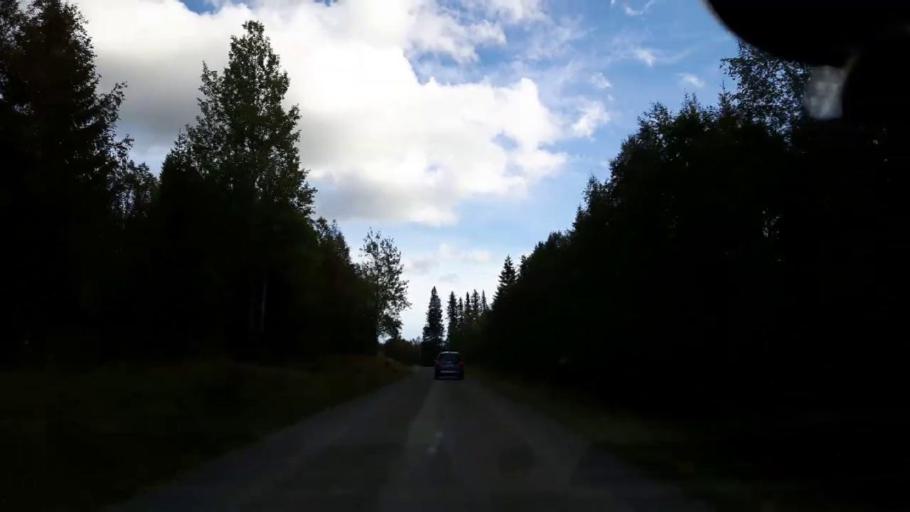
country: SE
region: Jaemtland
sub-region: Ragunda Kommun
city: Hammarstrand
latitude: 63.4154
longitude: 16.0791
